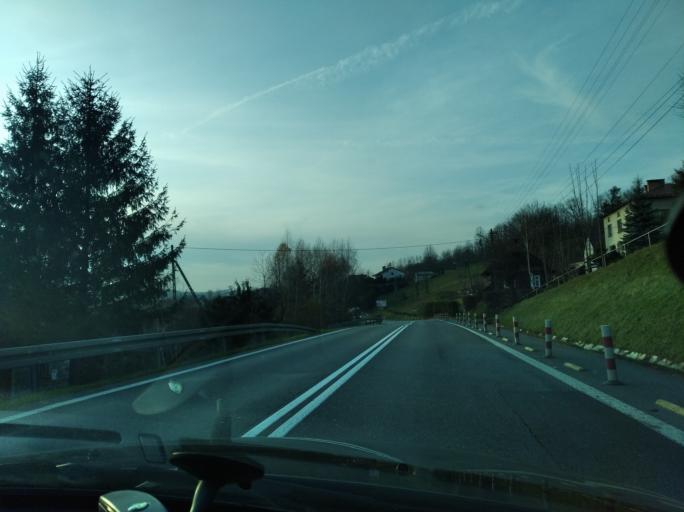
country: PL
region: Subcarpathian Voivodeship
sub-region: Powiat strzyzowski
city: Jawornik
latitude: 49.8052
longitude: 21.9015
